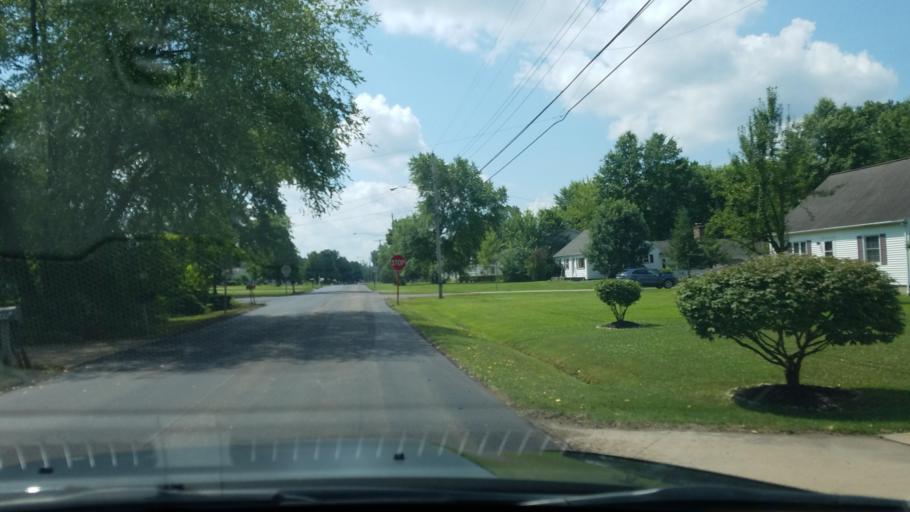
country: US
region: Ohio
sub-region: Trumbull County
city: Champion Heights
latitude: 41.3012
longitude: -80.8635
